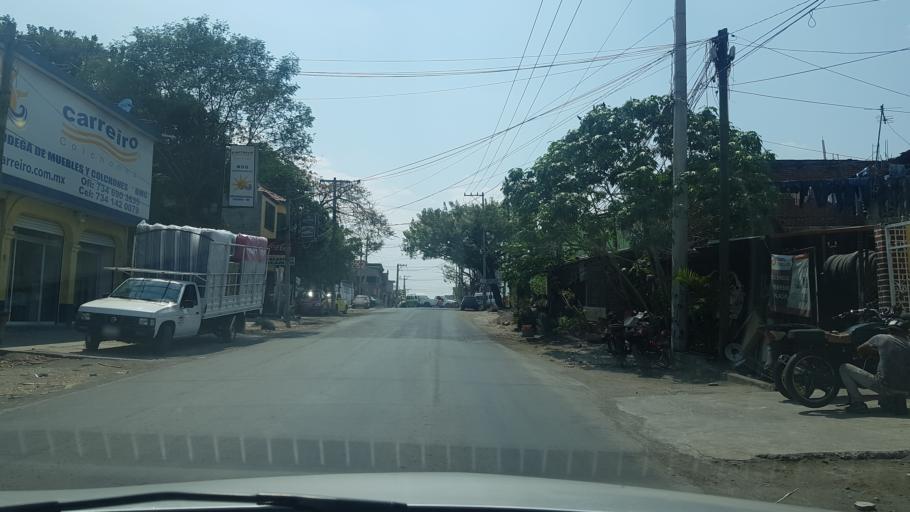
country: MX
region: Morelos
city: Zacatepec
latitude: 18.6586
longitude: -99.1856
